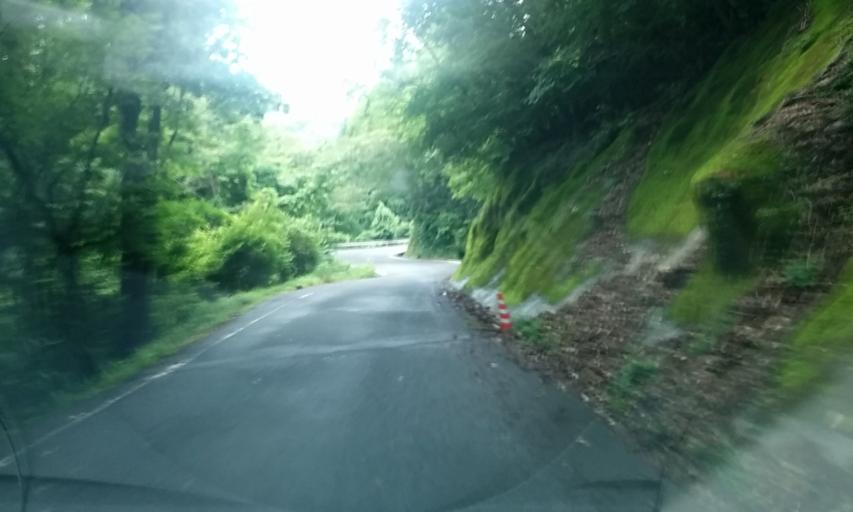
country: JP
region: Kyoto
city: Kameoka
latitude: 35.0516
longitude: 135.4256
